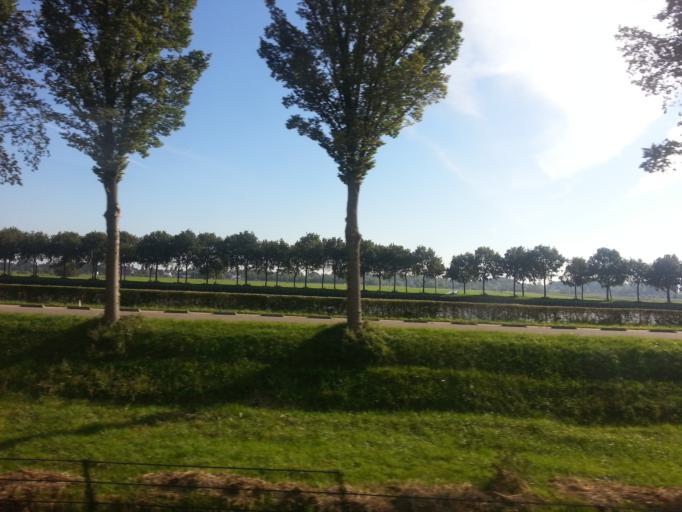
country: NL
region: Utrecht
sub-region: Stichtse Vecht
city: Breukelen
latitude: 52.2093
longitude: 5.0009
